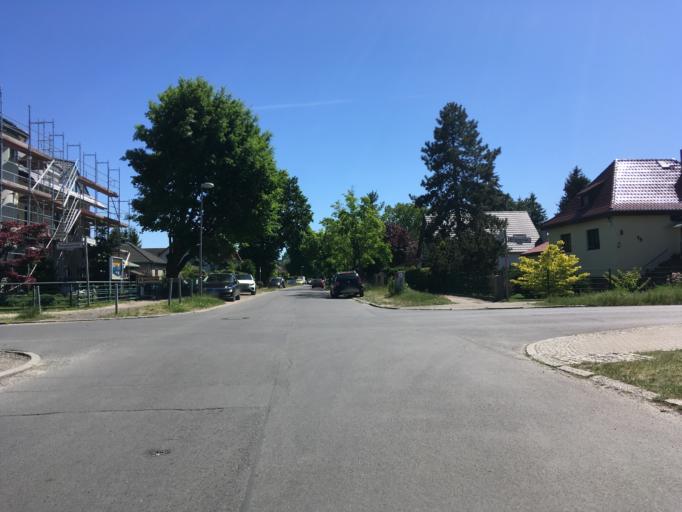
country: DE
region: Berlin
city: Berlin Koepenick
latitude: 52.4325
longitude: 13.5915
